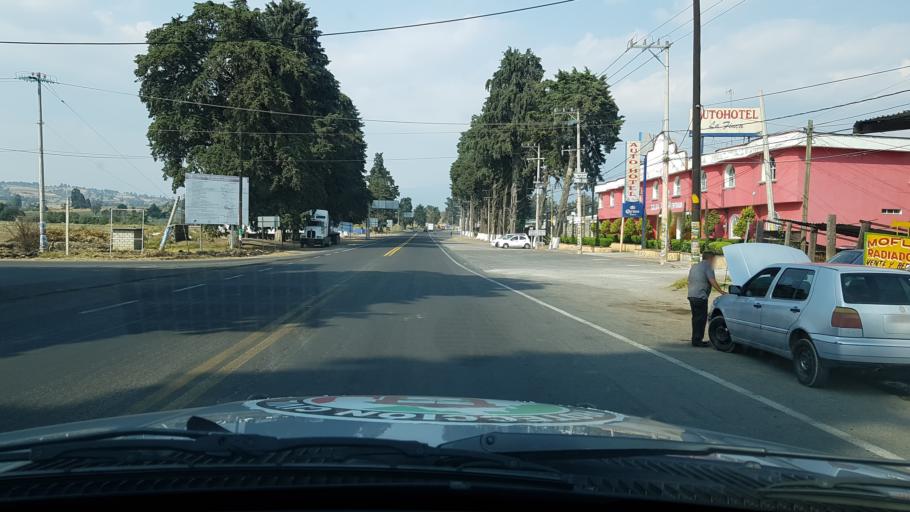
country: MX
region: Mexico
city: Tepetlixpa
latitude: 19.0351
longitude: -98.8095
